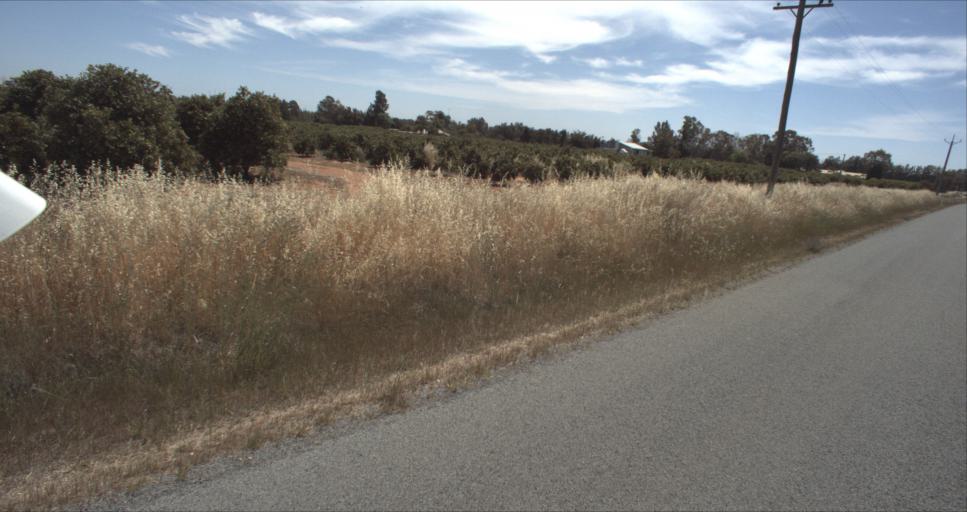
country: AU
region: New South Wales
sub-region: Leeton
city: Leeton
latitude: -34.5763
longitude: 146.4304
